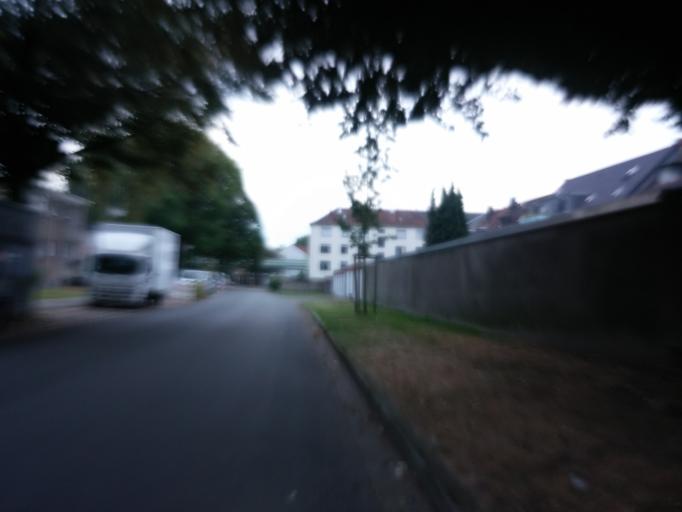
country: DE
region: North Rhine-Westphalia
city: Marl
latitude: 51.5996
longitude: 7.0512
